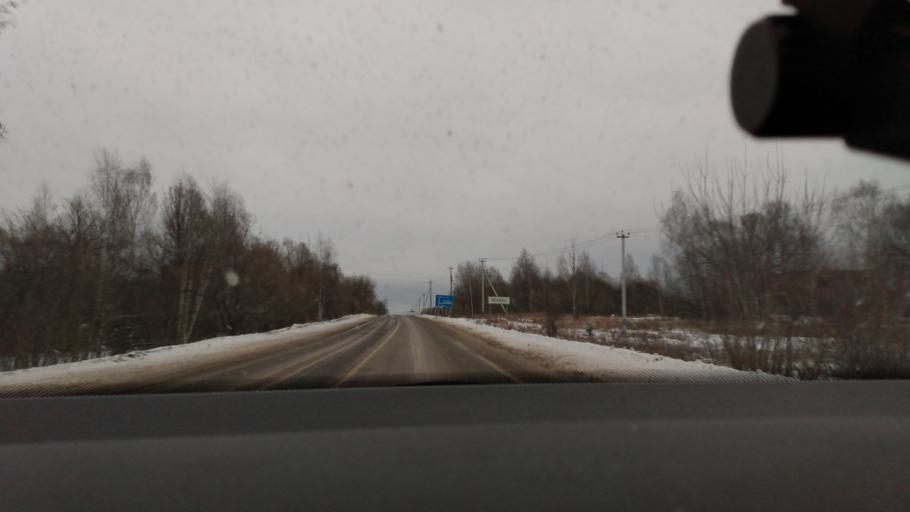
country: RU
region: Moskovskaya
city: Krasnaya Poyma
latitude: 55.1630
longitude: 39.2147
